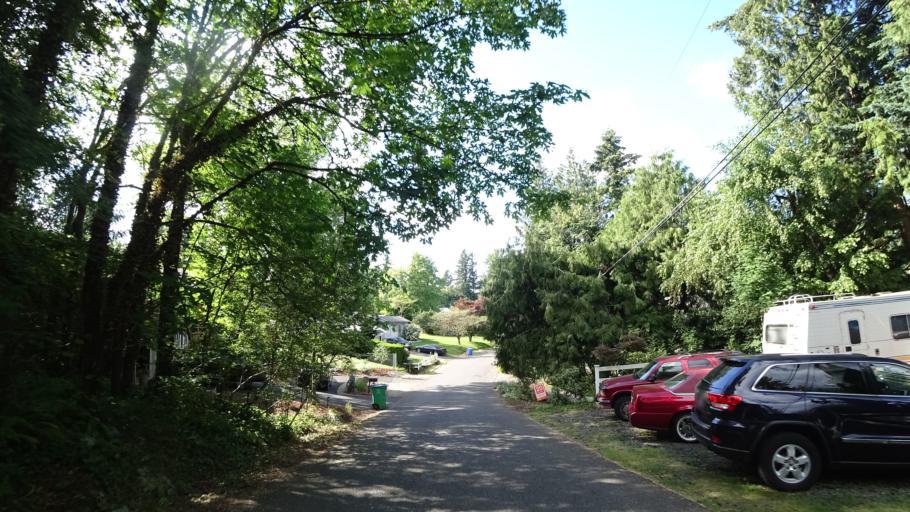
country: US
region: Oregon
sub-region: Washington County
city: Raleigh Hills
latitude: 45.4820
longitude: -122.7169
